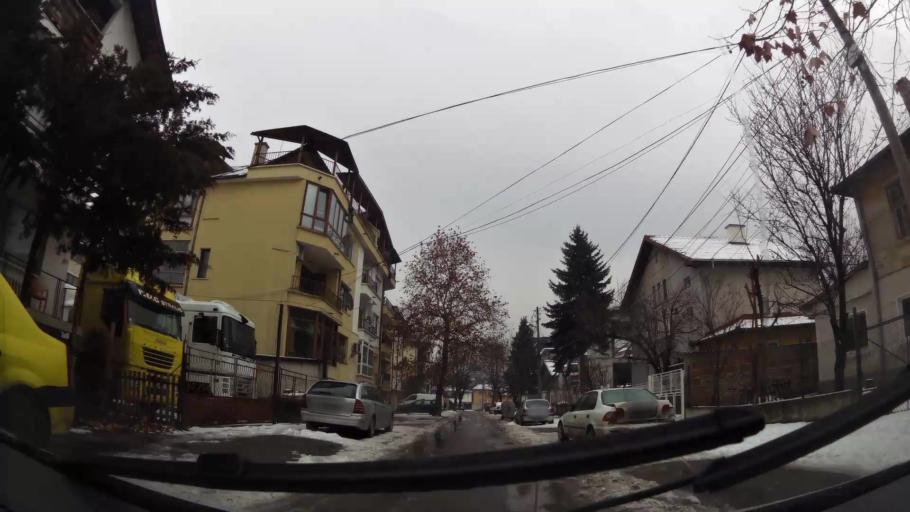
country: BG
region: Sofia-Capital
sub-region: Stolichna Obshtina
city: Sofia
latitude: 42.6756
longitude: 23.2657
